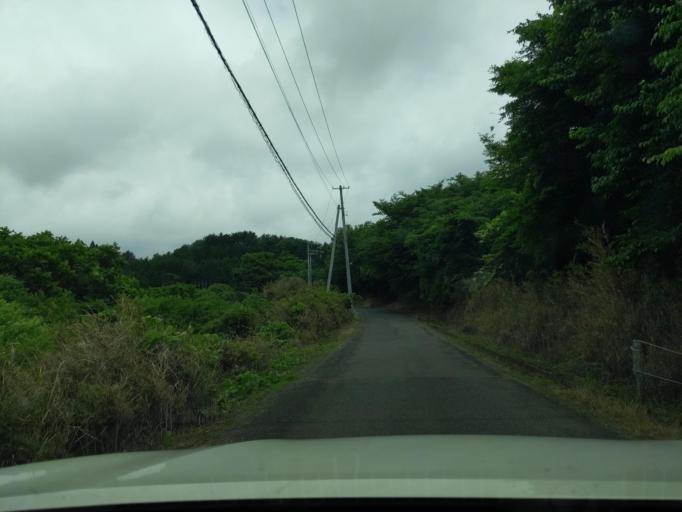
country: JP
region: Fukushima
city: Koriyama
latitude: 37.4624
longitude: 140.3085
